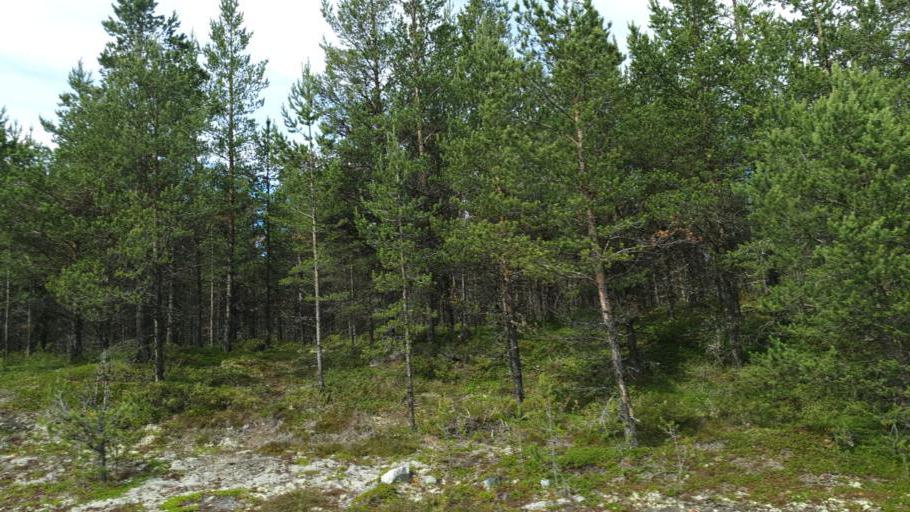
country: NO
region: Oppland
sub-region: Vaga
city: Vagamo
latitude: 61.7190
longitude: 9.0558
